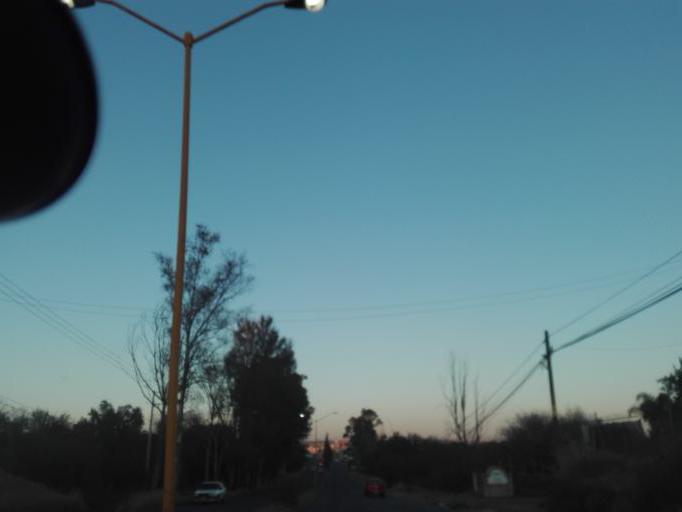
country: MX
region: Aguascalientes
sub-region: Aguascalientes
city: La Loma de los Negritos
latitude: 21.8648
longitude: -102.3332
